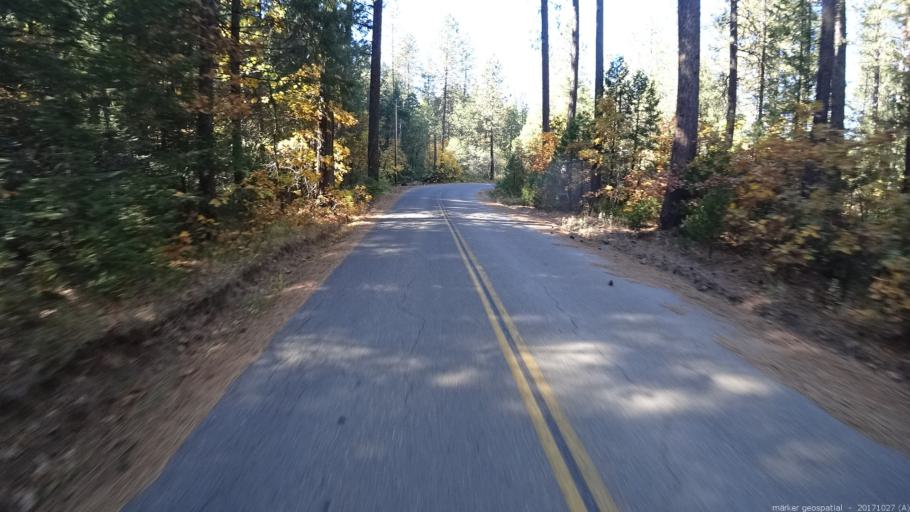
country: US
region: California
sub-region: Shasta County
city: Shingletown
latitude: 40.7376
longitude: -121.9262
